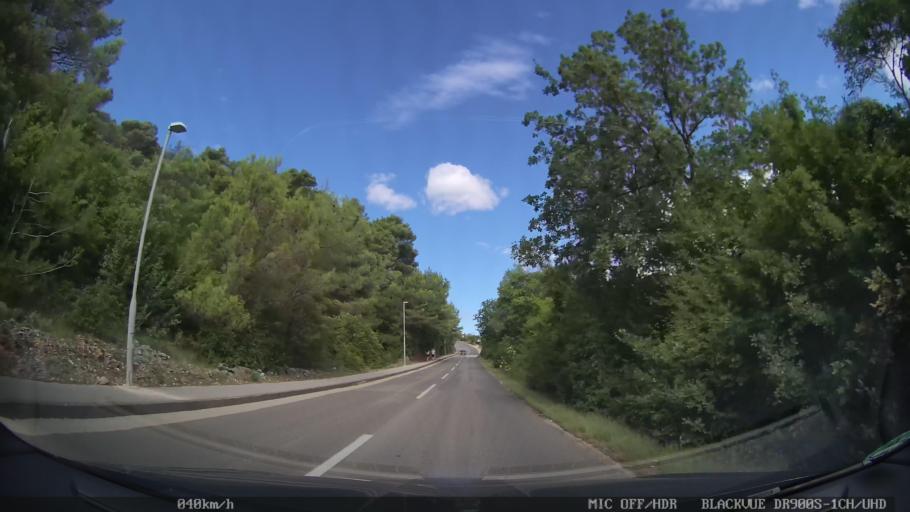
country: HR
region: Primorsko-Goranska
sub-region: Grad Krk
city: Krk
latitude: 45.0482
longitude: 14.5364
